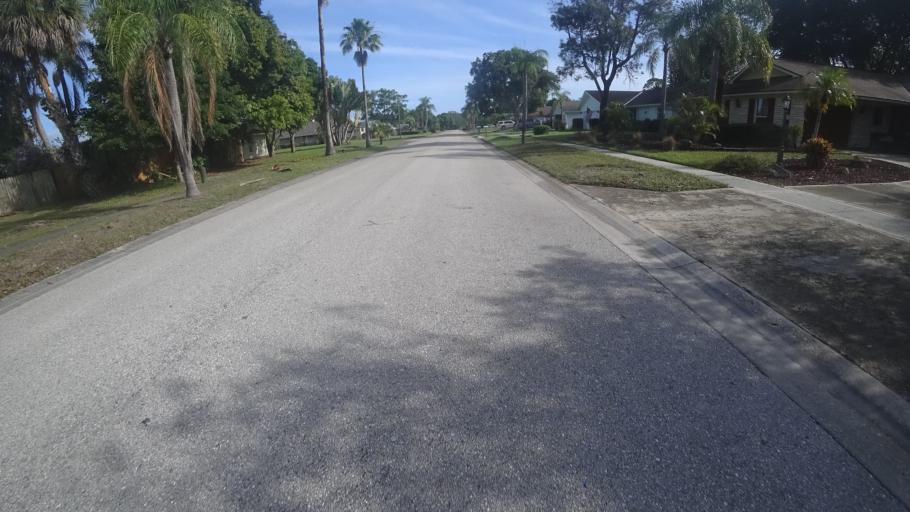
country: US
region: Florida
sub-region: Manatee County
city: West Bradenton
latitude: 27.5007
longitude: -82.6244
